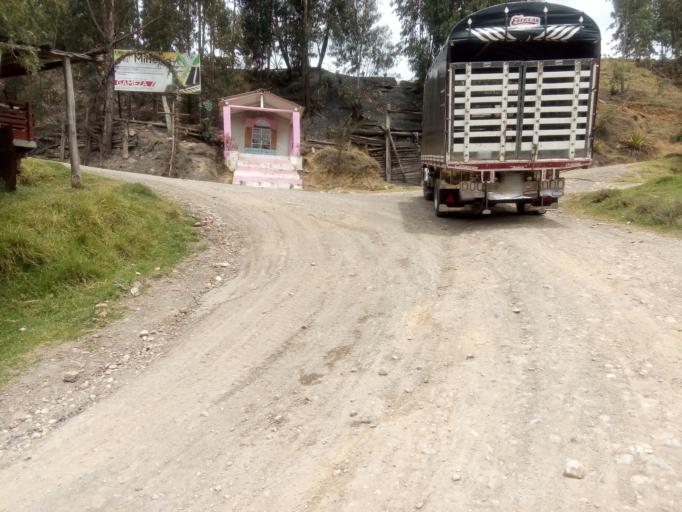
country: CO
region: Boyaca
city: Gameza
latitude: 5.8086
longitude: -72.8024
